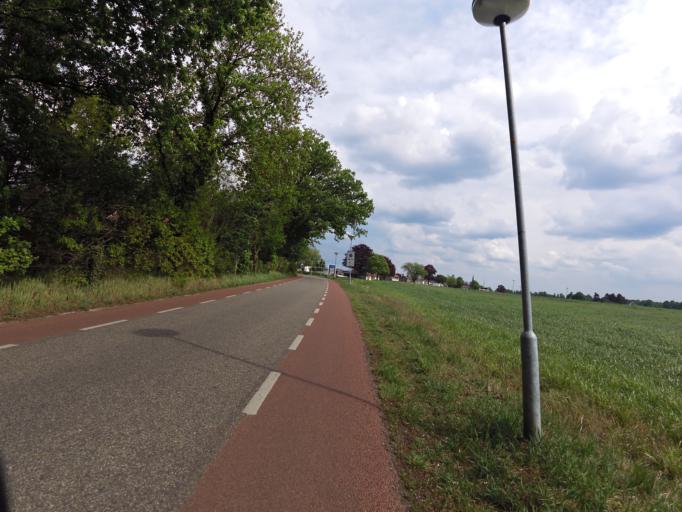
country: NL
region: Gelderland
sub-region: Gemeente Montferland
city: s-Heerenberg
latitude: 51.8810
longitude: 6.2350
